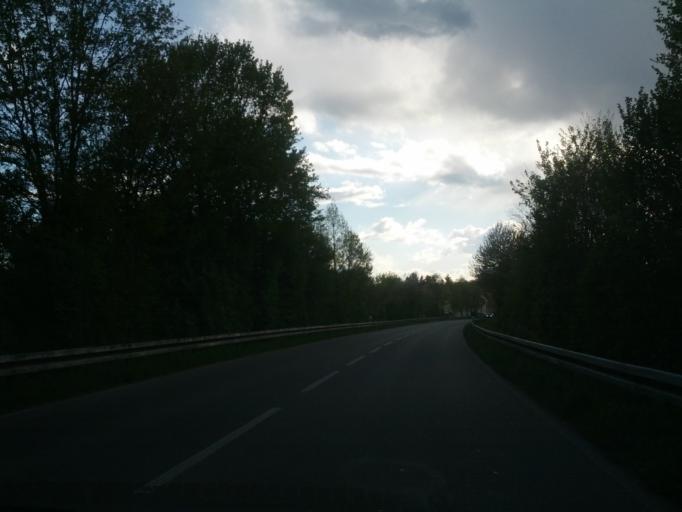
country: DE
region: Baden-Wuerttemberg
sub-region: Freiburg Region
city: Vorstetten
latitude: 48.0726
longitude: 7.8075
